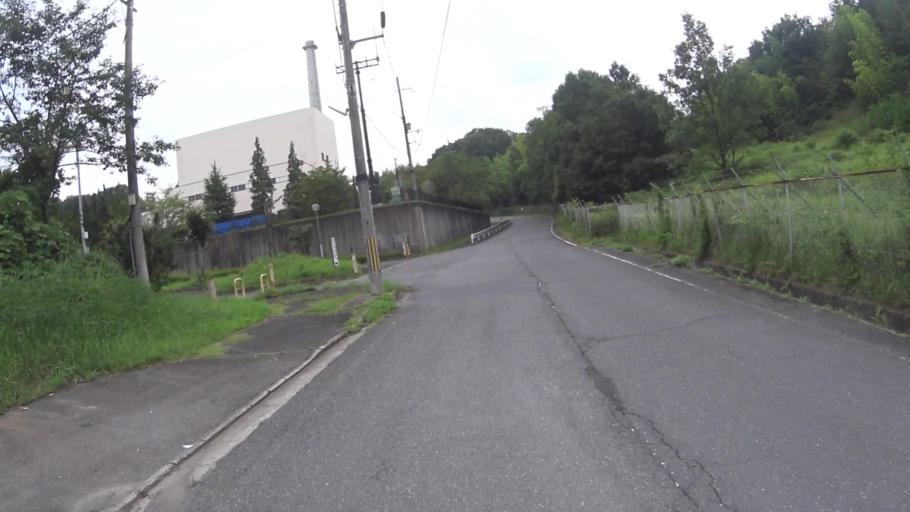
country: JP
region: Kyoto
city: Tanabe
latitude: 34.7693
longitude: 135.7738
